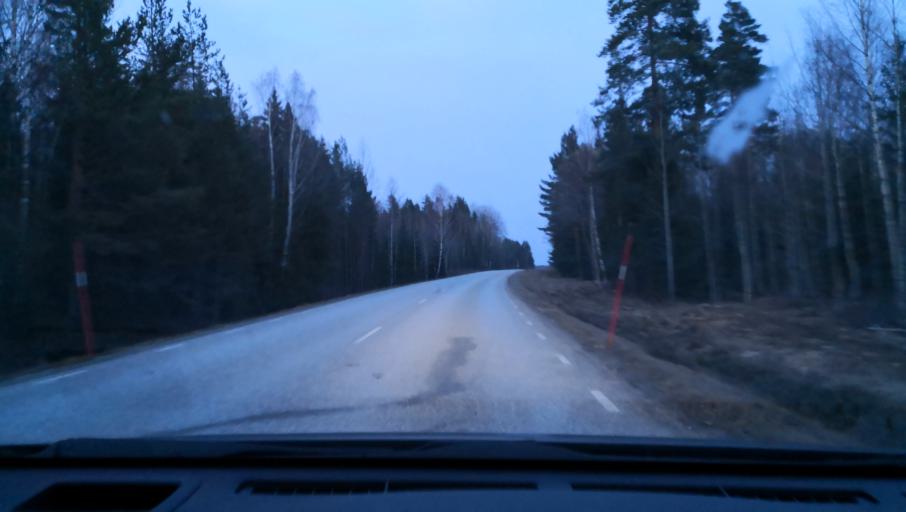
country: SE
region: OErebro
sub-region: Lindesbergs Kommun
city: Lindesberg
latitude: 59.5974
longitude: 15.3307
